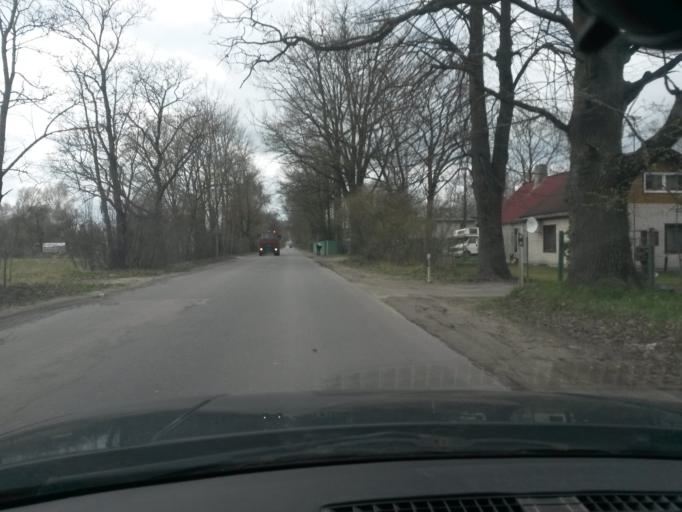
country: LV
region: Kekava
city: Kekava
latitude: 56.8947
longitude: 24.2374
